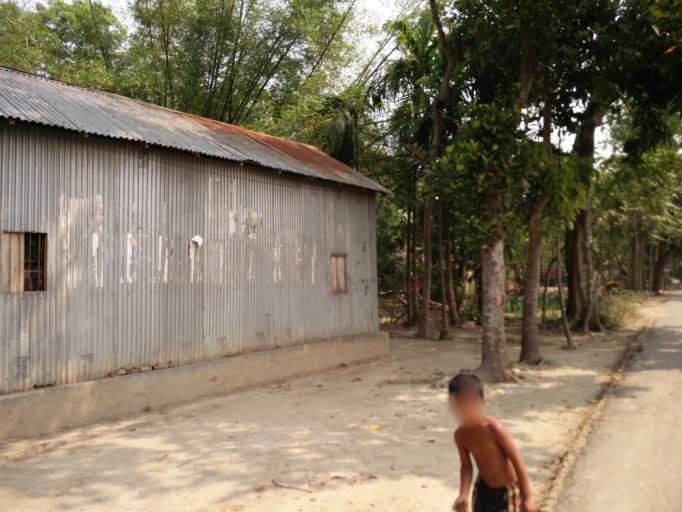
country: BD
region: Dhaka
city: Muktagacha
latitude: 24.9246
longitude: 90.2446
